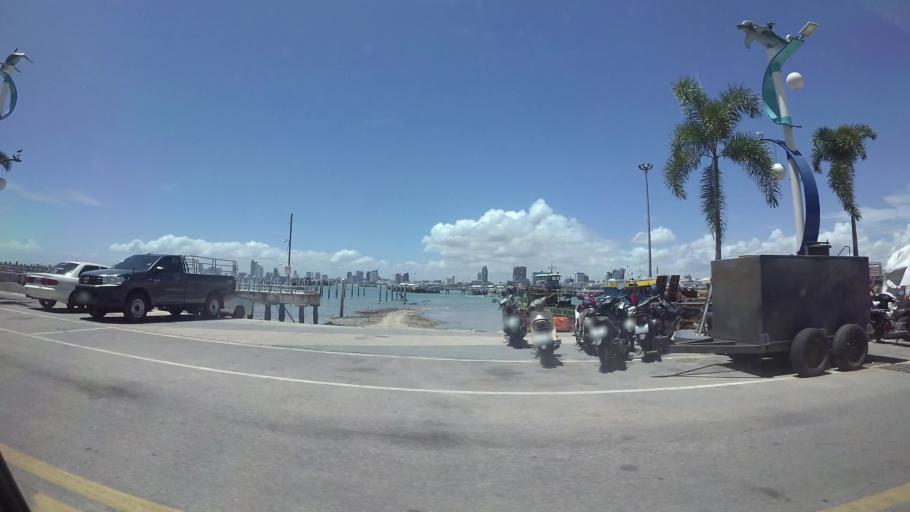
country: TH
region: Chon Buri
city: Phatthaya
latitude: 12.9275
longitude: 100.8641
